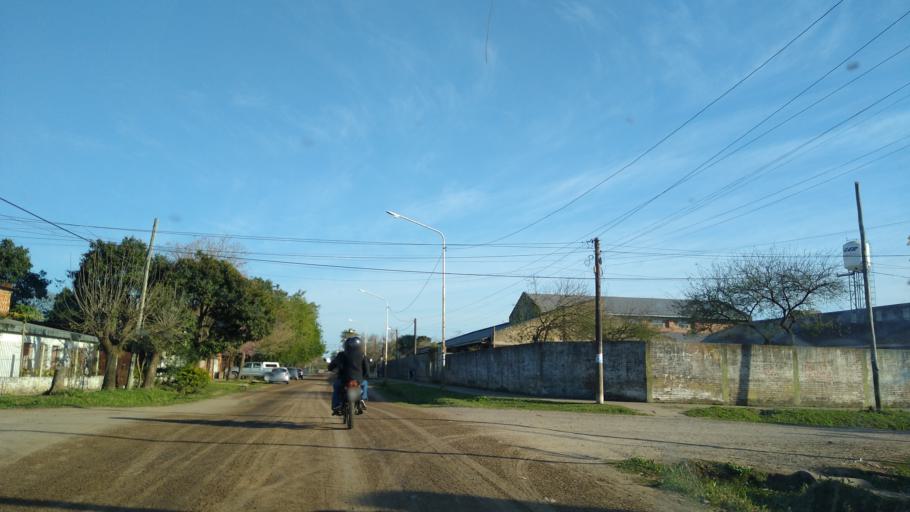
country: AR
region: Chaco
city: Barranqueras
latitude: -27.4720
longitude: -58.9325
